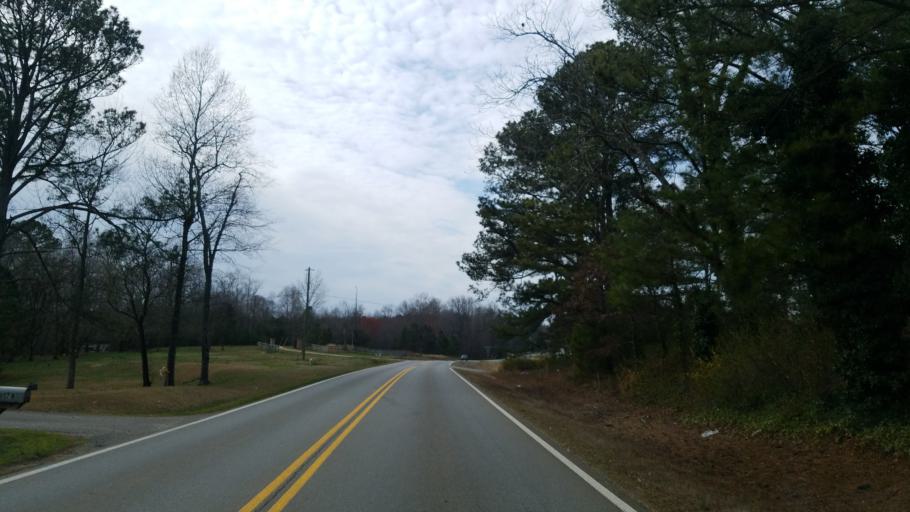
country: US
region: Georgia
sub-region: Cherokee County
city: Ball Ground
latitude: 34.3052
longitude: -84.3296
